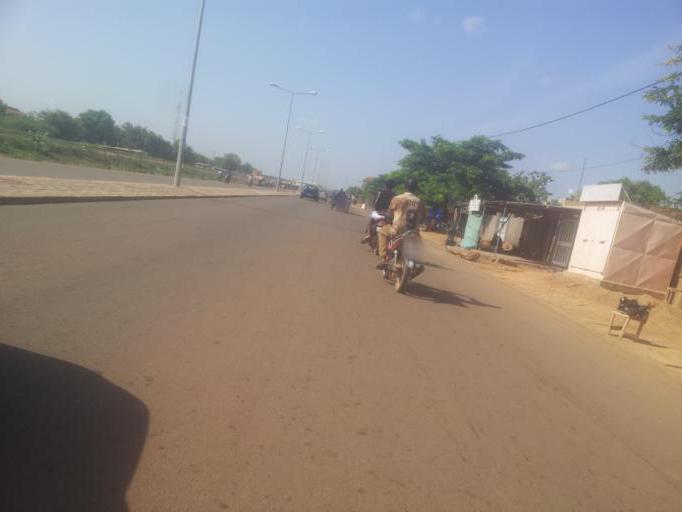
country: BF
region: Centre
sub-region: Kadiogo Province
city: Ouagadougou
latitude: 12.3774
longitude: -1.5698
